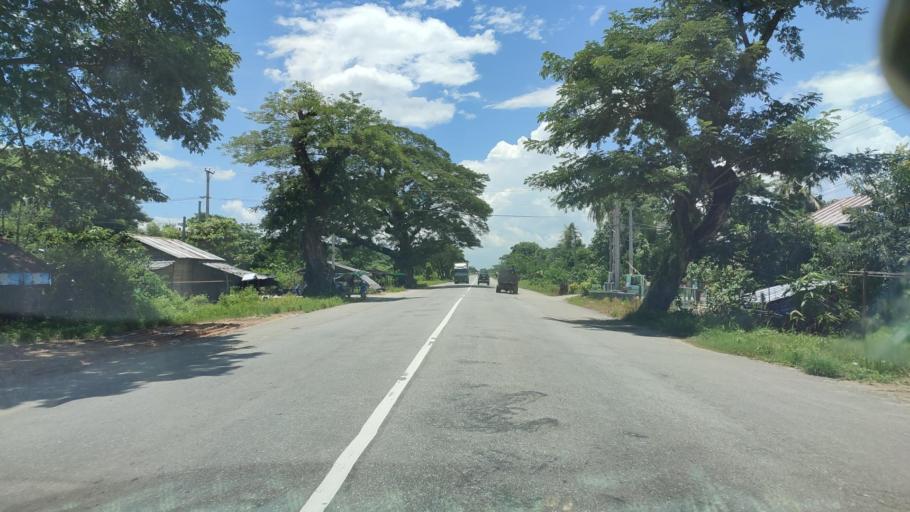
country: MM
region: Bago
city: Taungoo
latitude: 18.7228
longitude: 96.4077
